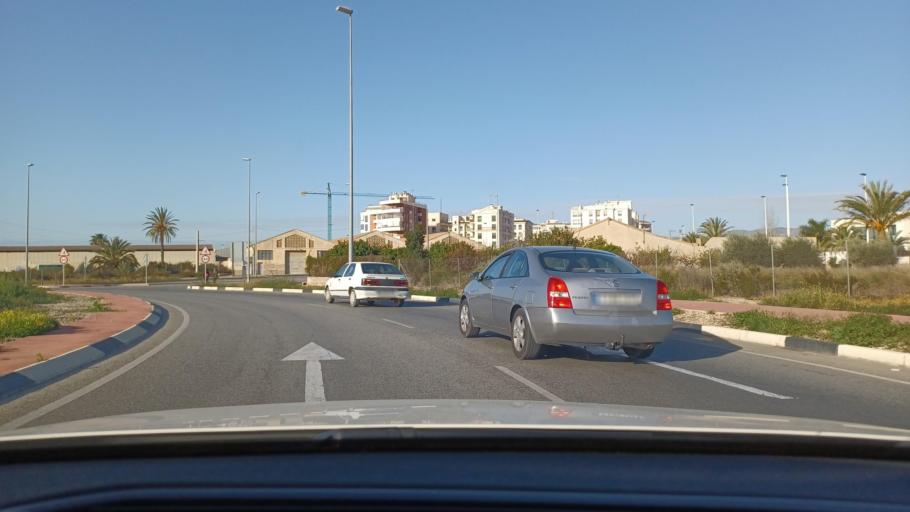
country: ES
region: Valencia
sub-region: Provincia de Alicante
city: Elche
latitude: 38.2530
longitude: -0.6923
